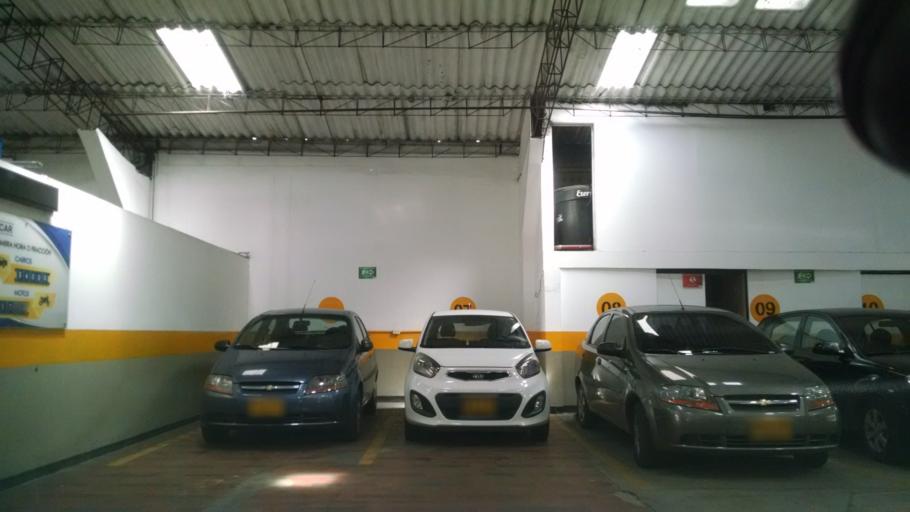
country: CO
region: Antioquia
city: Medellin
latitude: 6.2554
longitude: -75.5805
